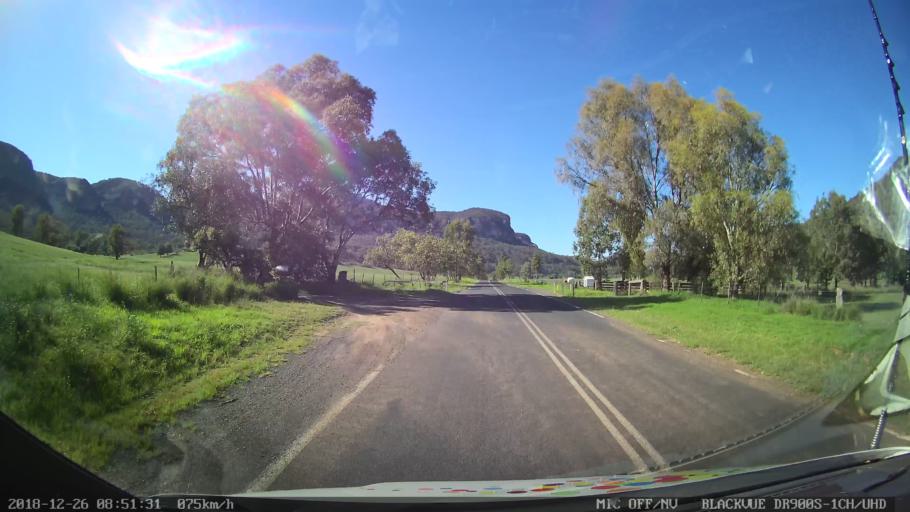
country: AU
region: New South Wales
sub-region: Mid-Western Regional
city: Kandos
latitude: -32.5853
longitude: 150.0884
